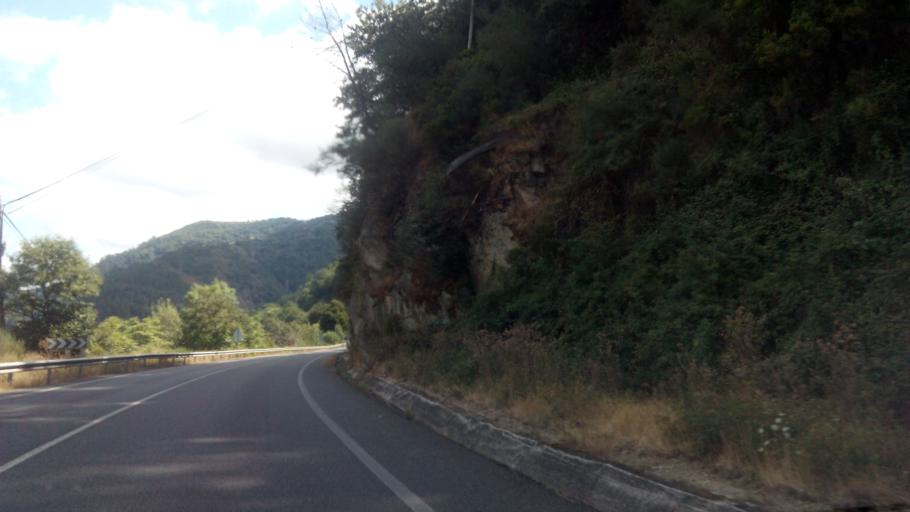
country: ES
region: Galicia
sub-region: Provincia de Ourense
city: Nogueira de Ramuin
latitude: 42.4456
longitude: -7.7388
